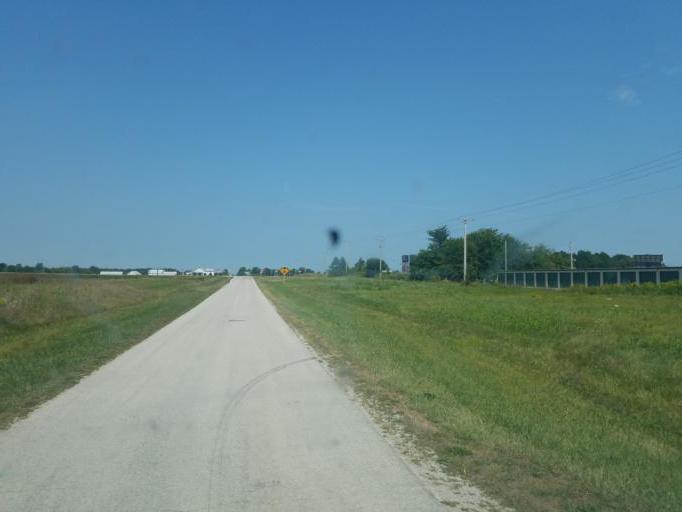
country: US
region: Ohio
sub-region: Crawford County
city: Bucyrus
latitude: 40.8076
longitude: -83.1122
